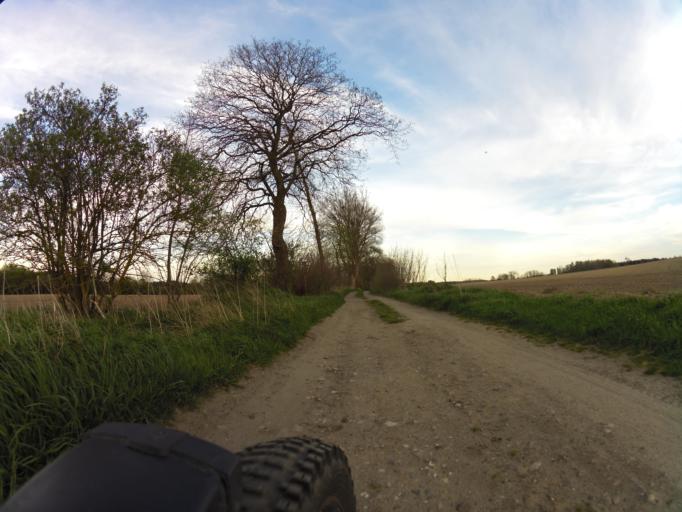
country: PL
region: West Pomeranian Voivodeship
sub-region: Powiat lobeski
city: Lobez
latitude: 53.7238
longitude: 15.6409
